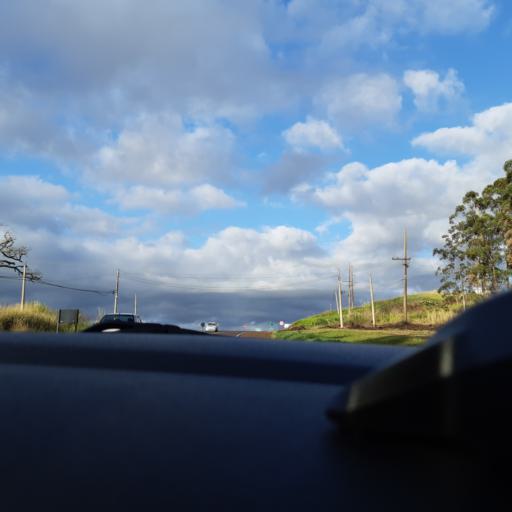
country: BR
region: Sao Paulo
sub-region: Ourinhos
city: Ourinhos
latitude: -22.9944
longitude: -49.8481
